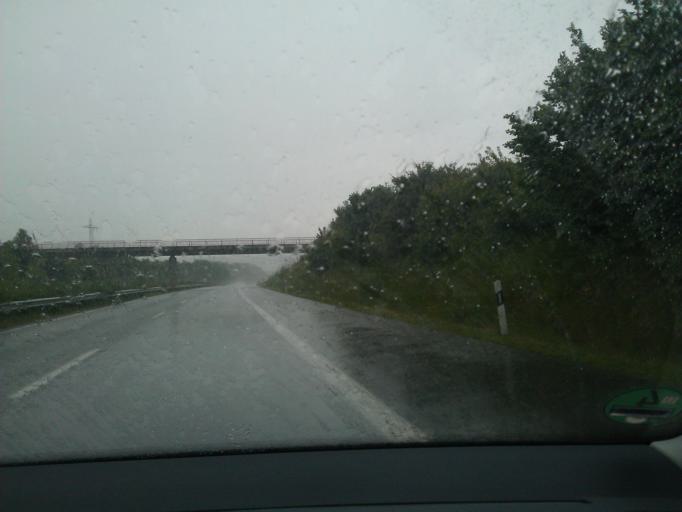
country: DE
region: Rheinland-Pfalz
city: Wilsecker
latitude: 50.0172
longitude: 6.5948
